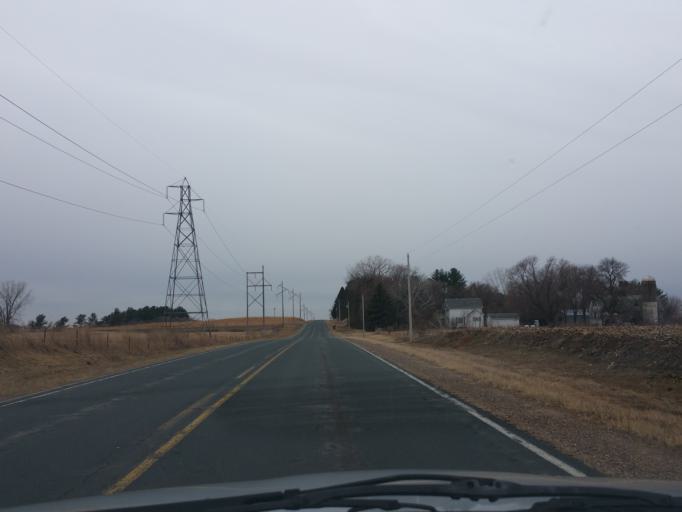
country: US
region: Wisconsin
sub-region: Saint Croix County
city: Roberts
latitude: 45.0357
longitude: -92.5739
